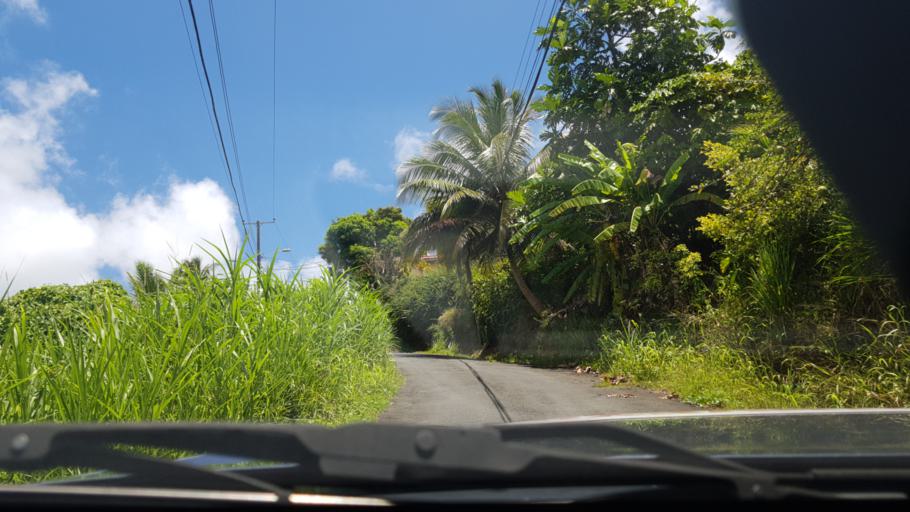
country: LC
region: Anse-la-Raye
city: Anse La Raye
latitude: 13.9561
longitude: -61.0000
